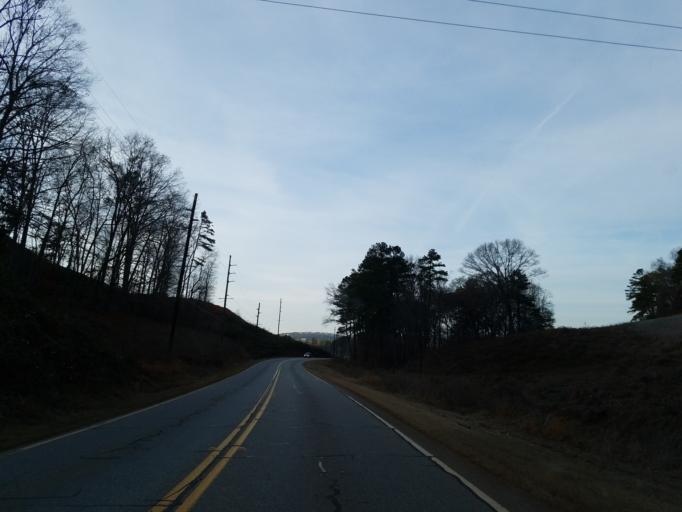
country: US
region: Georgia
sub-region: Bartow County
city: Emerson
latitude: 34.1398
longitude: -84.7636
